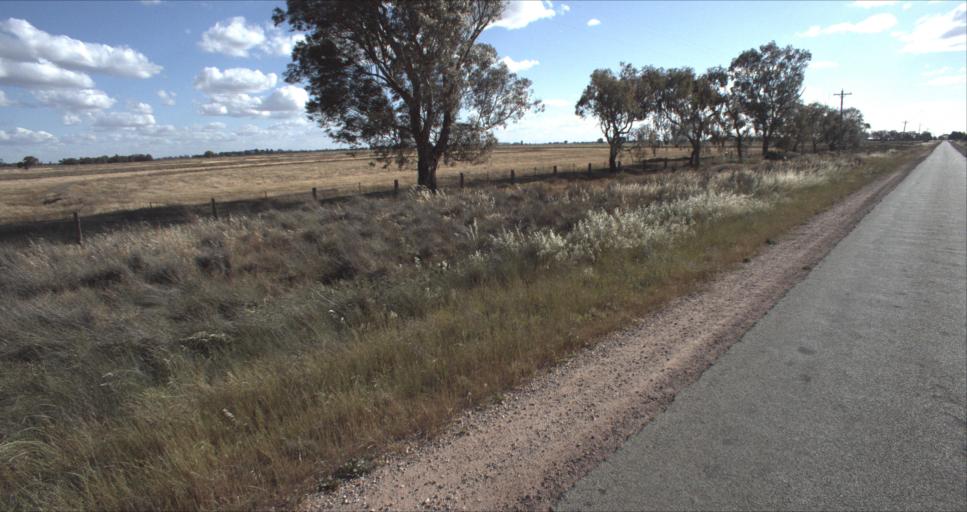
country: AU
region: New South Wales
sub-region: Leeton
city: Leeton
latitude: -34.4587
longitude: 146.2632
